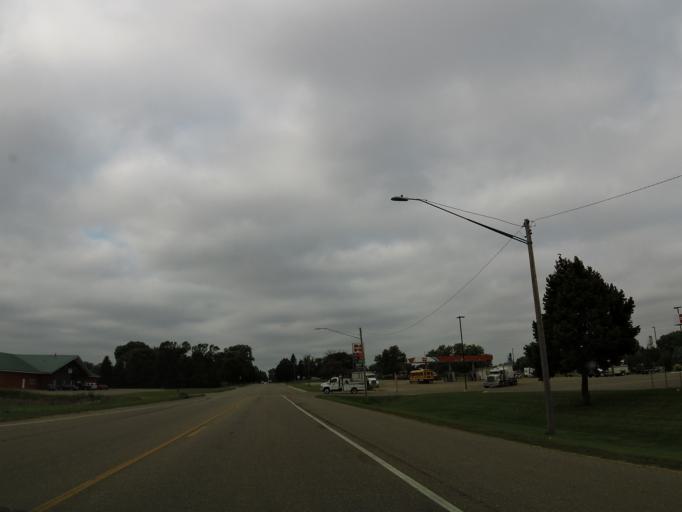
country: US
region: Minnesota
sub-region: Renville County
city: Renville
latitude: 44.7893
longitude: -95.1999
